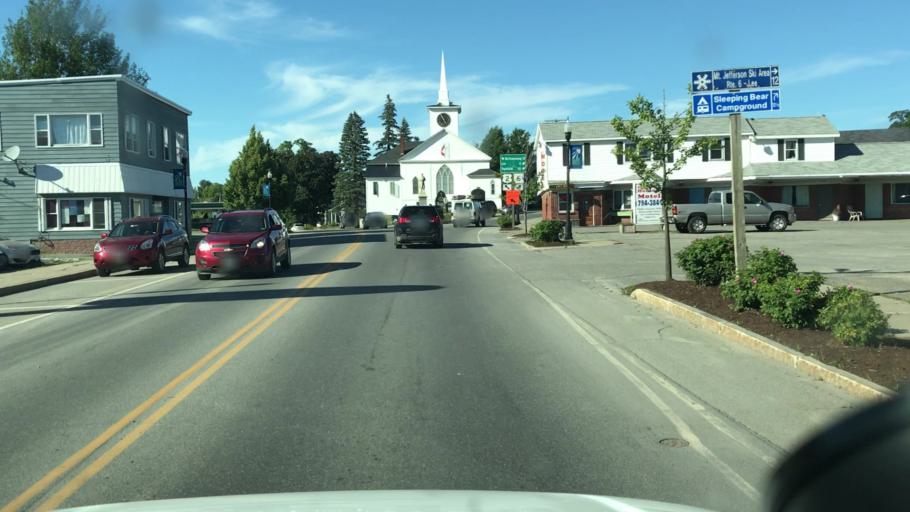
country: US
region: Maine
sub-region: Penobscot County
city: Lincoln
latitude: 45.3645
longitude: -68.5035
